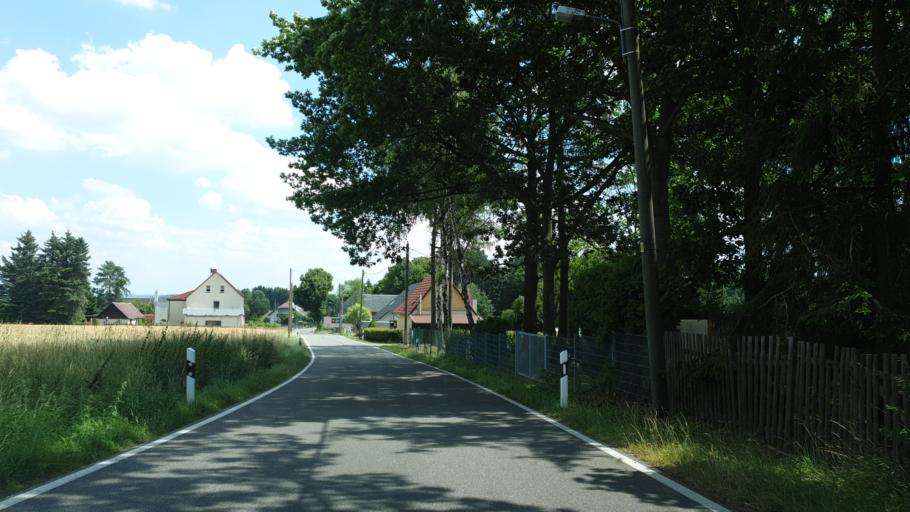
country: DE
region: Saxony
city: Kirchberg
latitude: 50.8027
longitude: 12.7712
